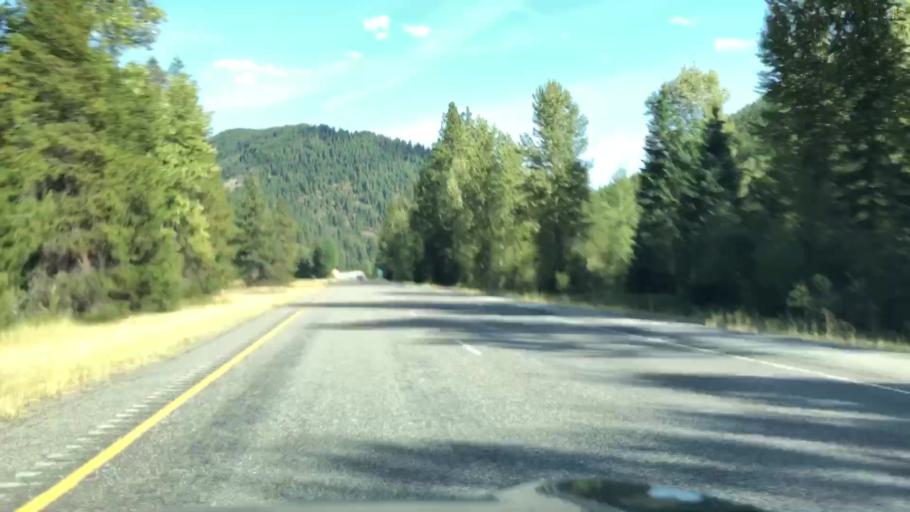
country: US
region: Montana
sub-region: Sanders County
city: Thompson Falls
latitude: 47.3581
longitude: -115.3077
